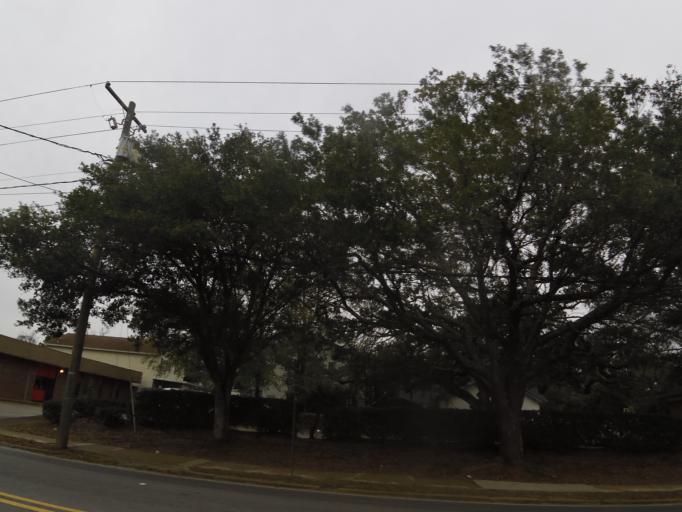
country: US
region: Georgia
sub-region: Thomas County
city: Thomasville
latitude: 30.8417
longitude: -83.9855
